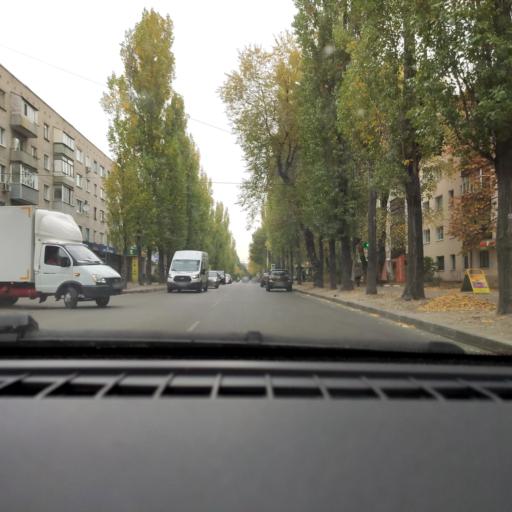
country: RU
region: Voronezj
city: Voronezh
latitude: 51.6880
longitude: 39.2592
